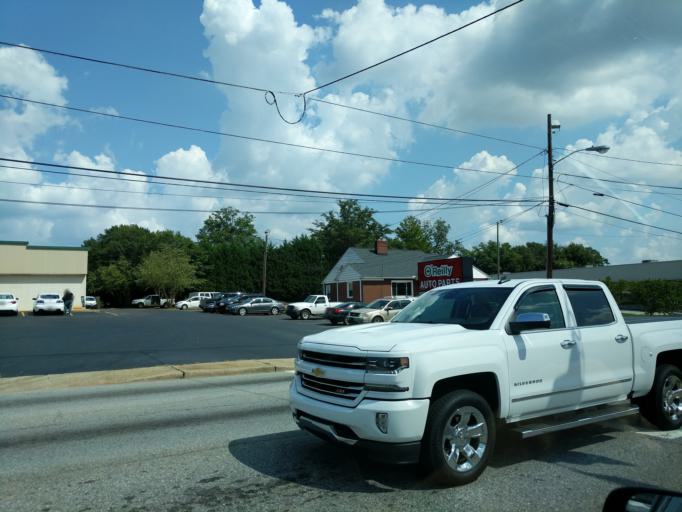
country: US
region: South Carolina
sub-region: Greenville County
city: Greenville
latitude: 34.8381
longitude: -82.3559
